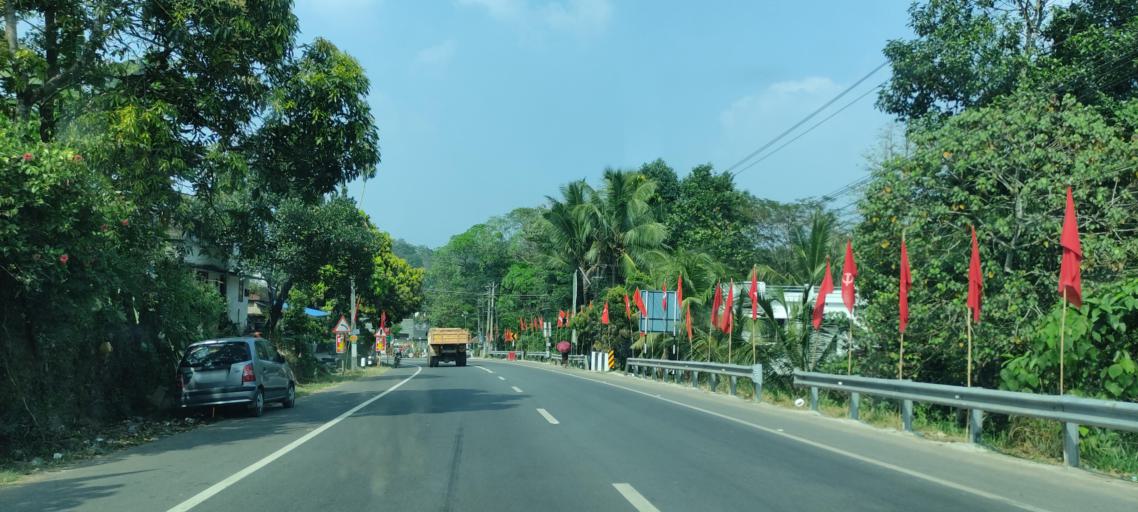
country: IN
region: Kerala
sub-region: Pattanamtitta
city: Adur
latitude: 9.1627
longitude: 76.7202
